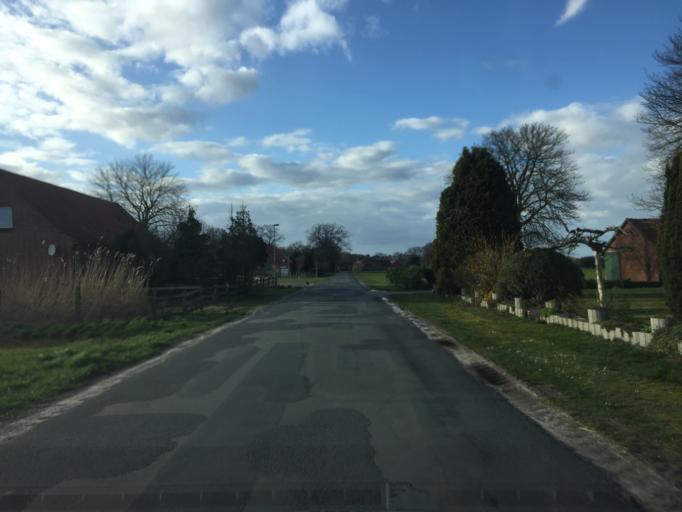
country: DE
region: Lower Saxony
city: Uchte
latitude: 52.5529
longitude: 8.9331
